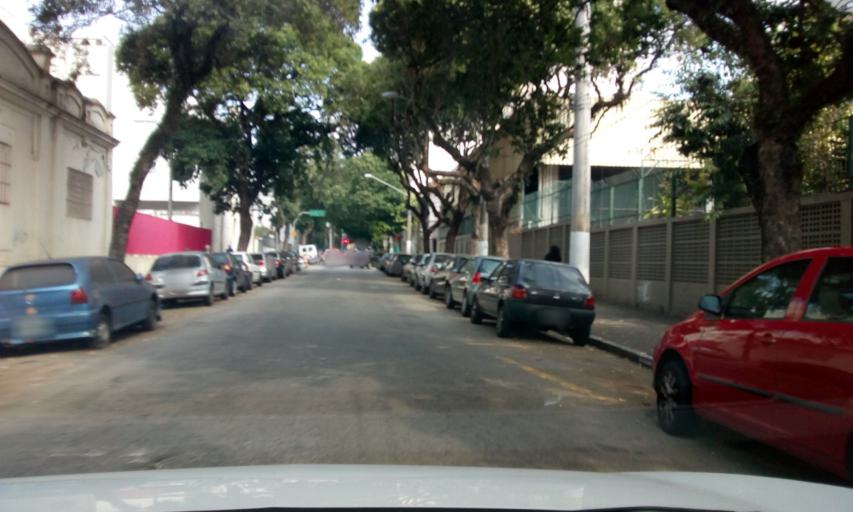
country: BR
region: Sao Paulo
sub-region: Sao Paulo
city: Sao Paulo
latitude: -23.5306
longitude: -46.6344
